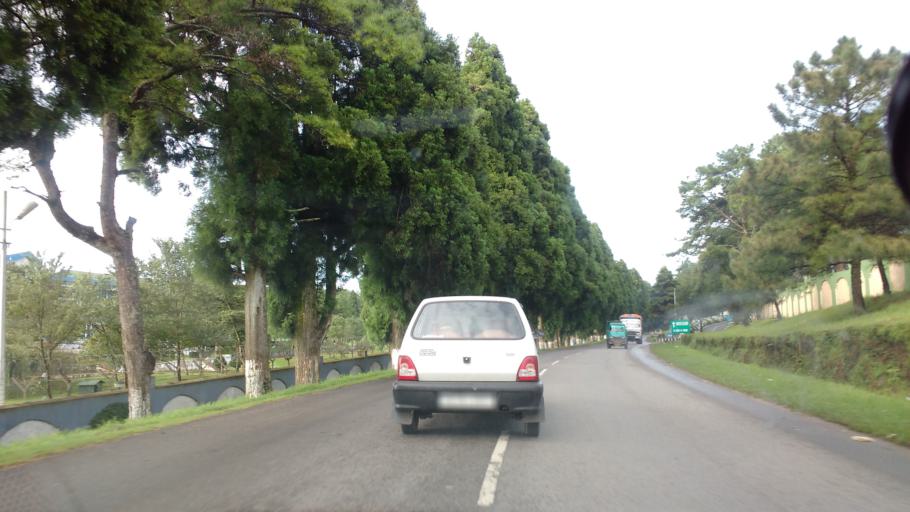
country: IN
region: Meghalaya
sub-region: East Khasi Hills
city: Shillong
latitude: 25.5403
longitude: 91.8291
